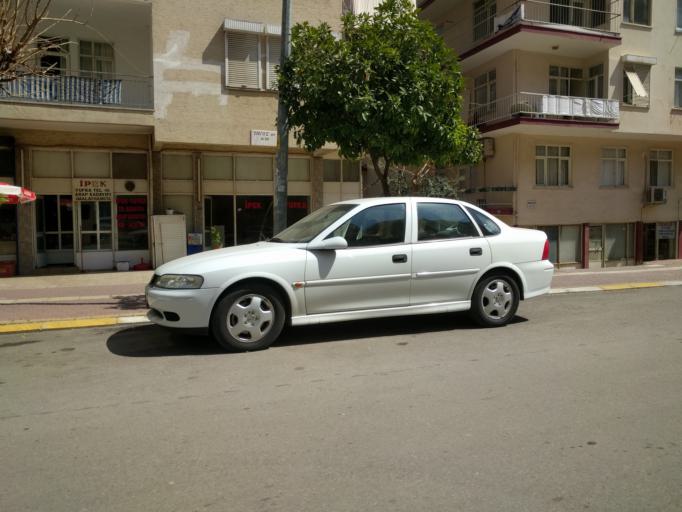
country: TR
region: Antalya
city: Antalya
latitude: 36.9099
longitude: 30.6830
